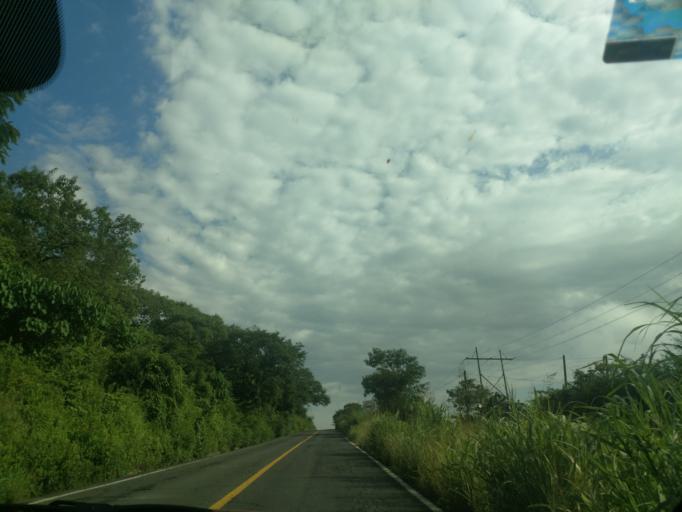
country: MX
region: Jalisco
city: Ameca
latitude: 20.5234
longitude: -104.1270
